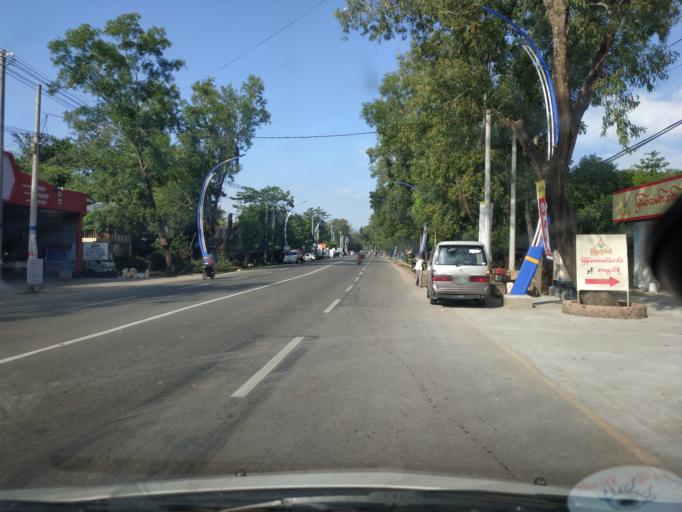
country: MM
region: Ayeyarwady
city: Pathein
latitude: 16.8022
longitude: 94.7674
